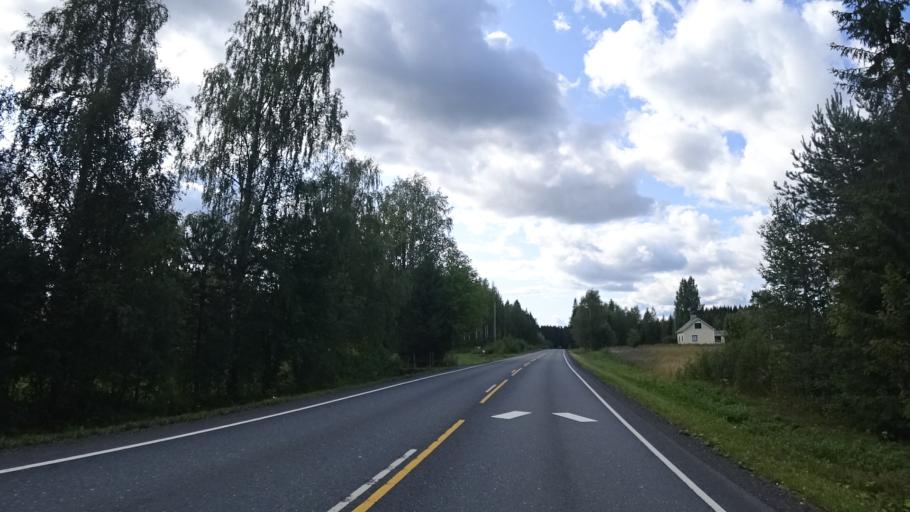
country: FI
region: North Karelia
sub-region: Keski-Karjala
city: Tohmajaervi
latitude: 62.1764
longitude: 30.5358
